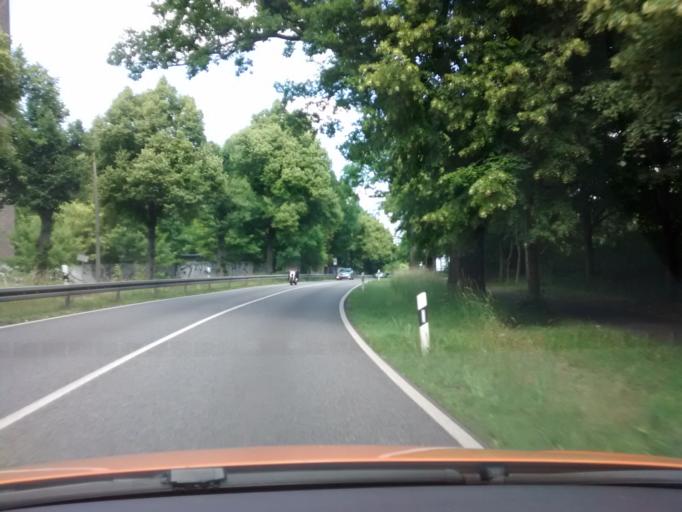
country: DE
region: Brandenburg
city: Potsdam
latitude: 52.4583
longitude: 13.0495
